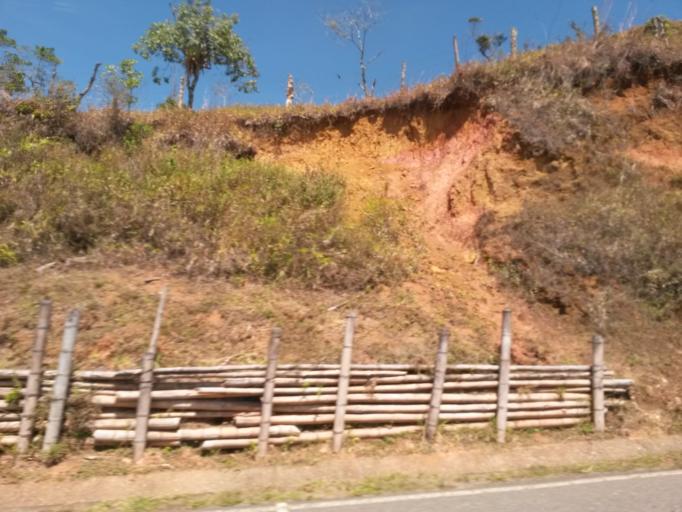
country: CO
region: Cauca
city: Lopez
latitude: 2.4399
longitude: -76.7827
